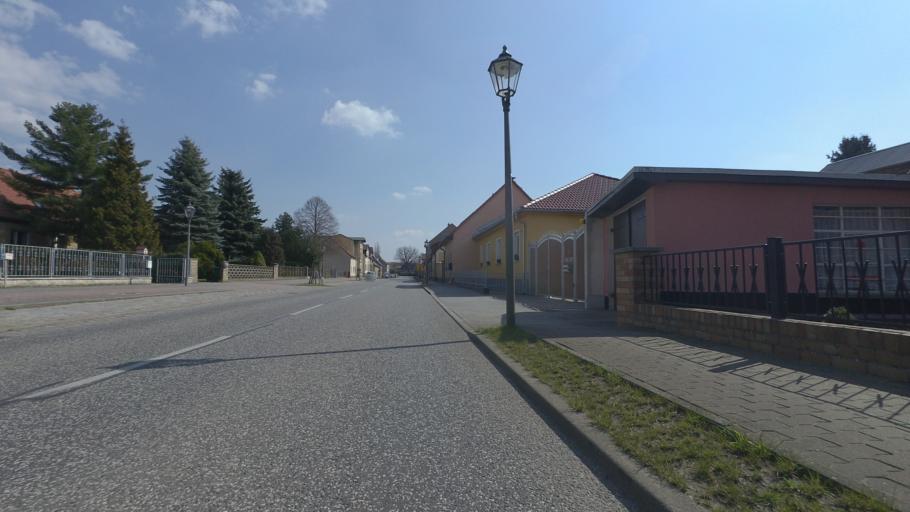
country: DE
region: Brandenburg
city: Mittenwalde
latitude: 52.2676
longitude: 13.5305
